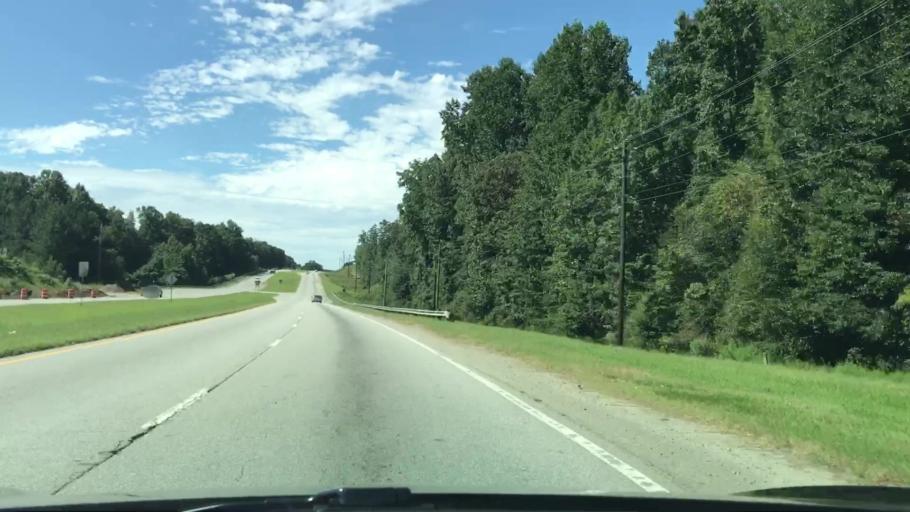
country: US
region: Georgia
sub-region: Gwinnett County
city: Buford
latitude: 34.1232
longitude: -84.0185
